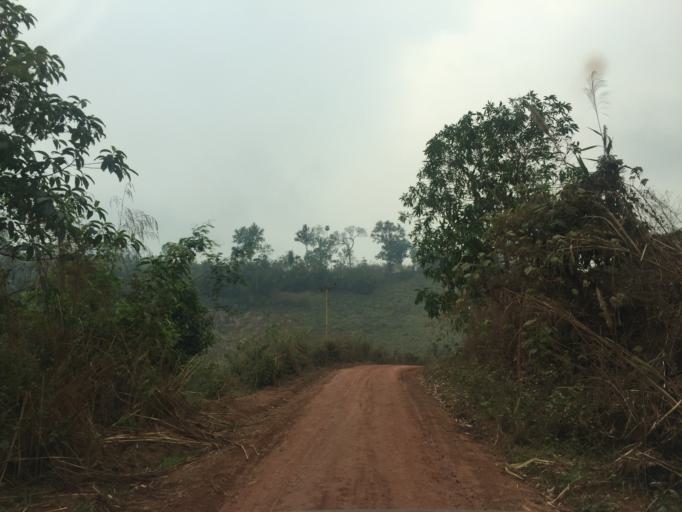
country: TH
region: Nan
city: Bo Kluea
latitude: 18.8468
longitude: 101.4175
